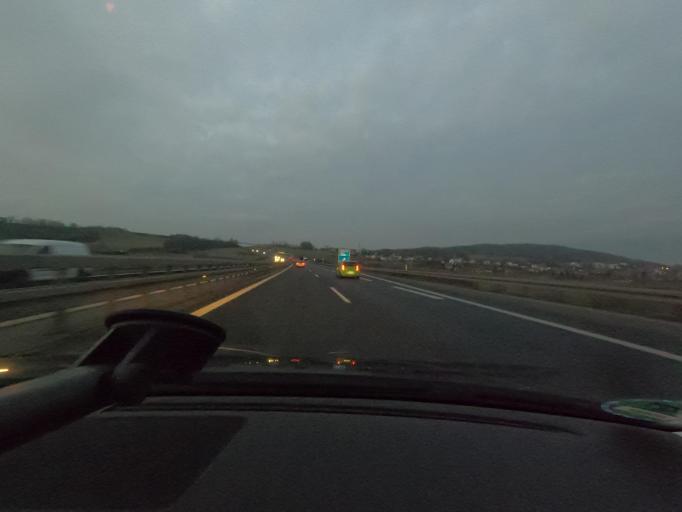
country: DE
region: Bavaria
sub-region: Upper Franconia
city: Lichtenfels
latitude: 50.1428
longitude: 11.0334
